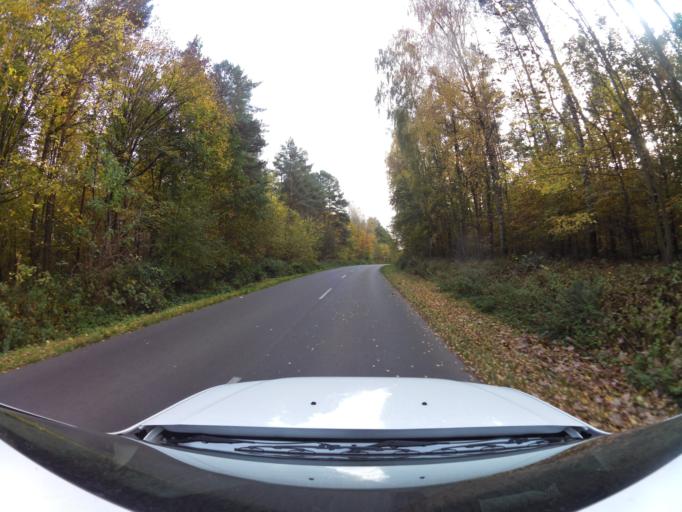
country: PL
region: West Pomeranian Voivodeship
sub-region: Powiat gryficki
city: Gryfice
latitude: 53.8622
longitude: 15.1165
